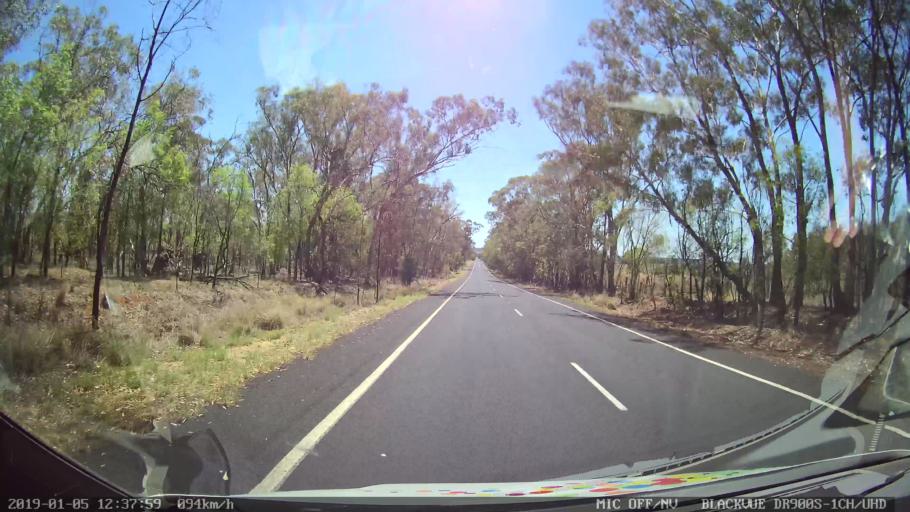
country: AU
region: New South Wales
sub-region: Warrumbungle Shire
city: Coonabarabran
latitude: -31.1994
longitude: 149.4623
